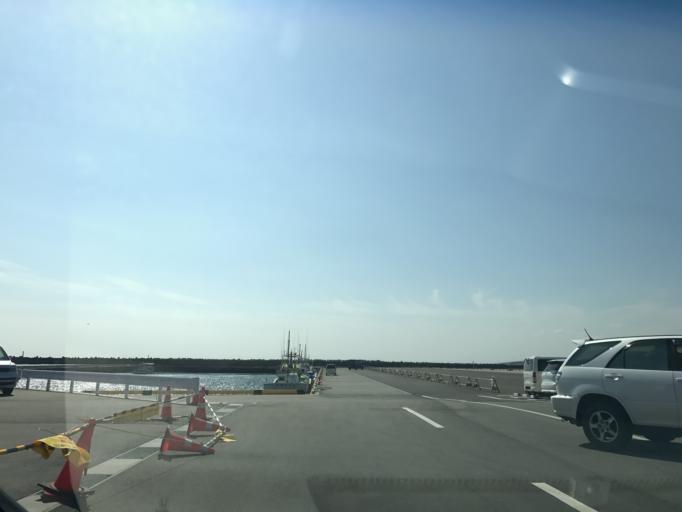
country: JP
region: Fukushima
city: Iwaki
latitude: 36.9425
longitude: 140.9062
